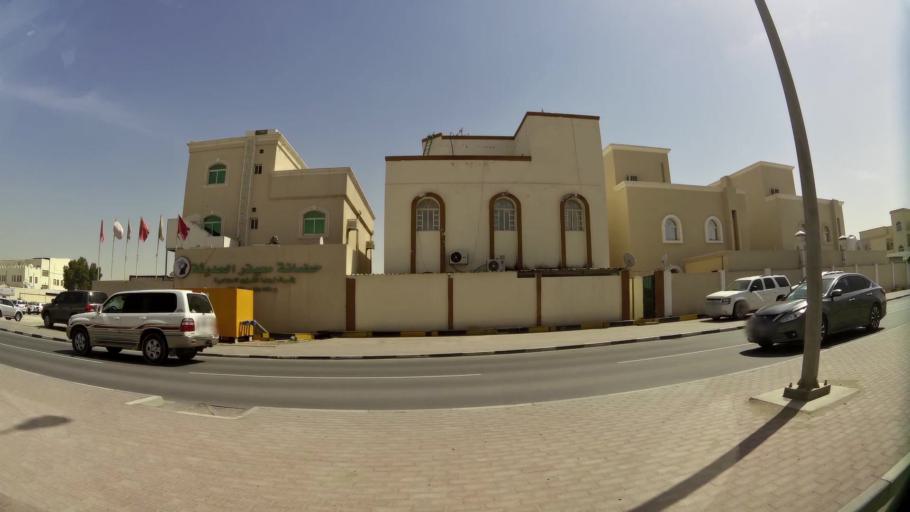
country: QA
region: Baladiyat ar Rayyan
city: Ar Rayyan
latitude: 25.2672
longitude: 51.4224
